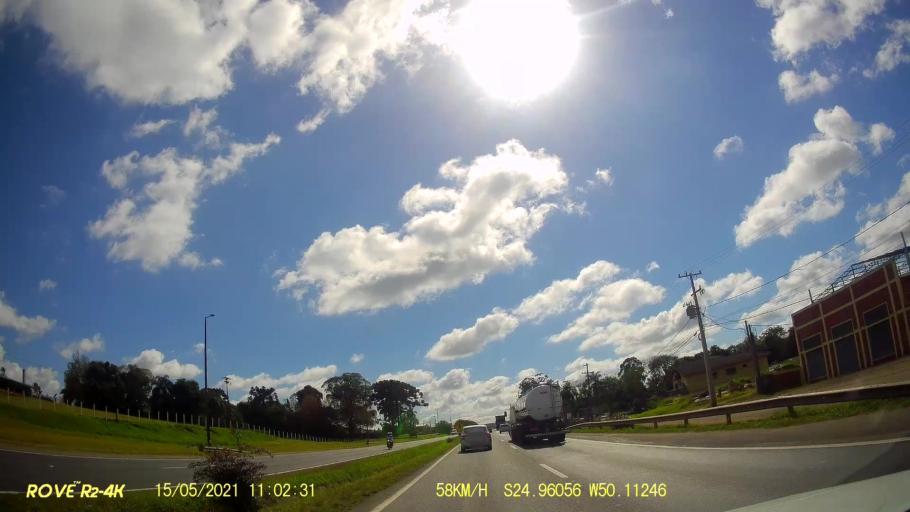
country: BR
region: Parana
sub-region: Carambei
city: Carambei
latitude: -24.9606
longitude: -50.1125
